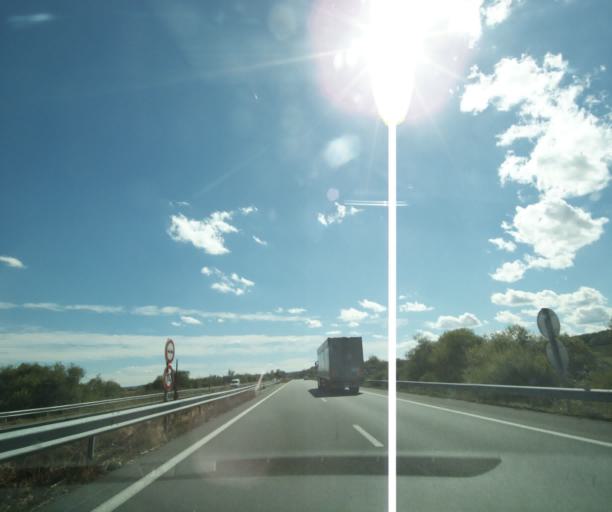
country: FR
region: Aquitaine
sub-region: Departement du Lot-et-Garonne
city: Damazan
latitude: 44.3120
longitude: 0.2597
